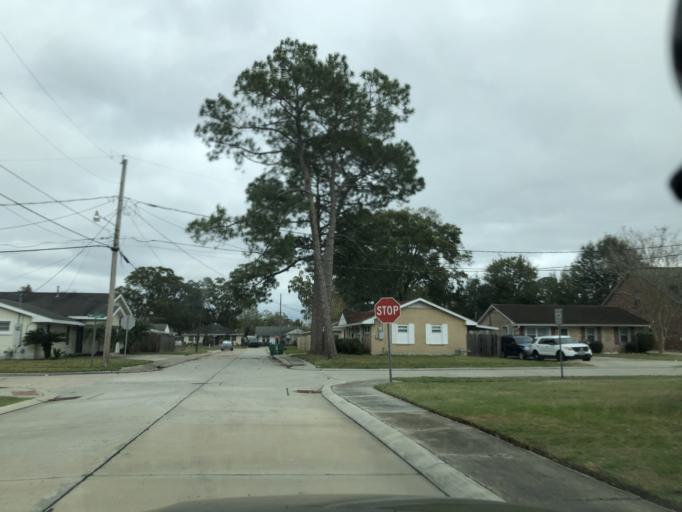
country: US
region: Louisiana
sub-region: Jefferson Parish
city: Metairie Terrace
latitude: 29.9837
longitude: -90.1656
